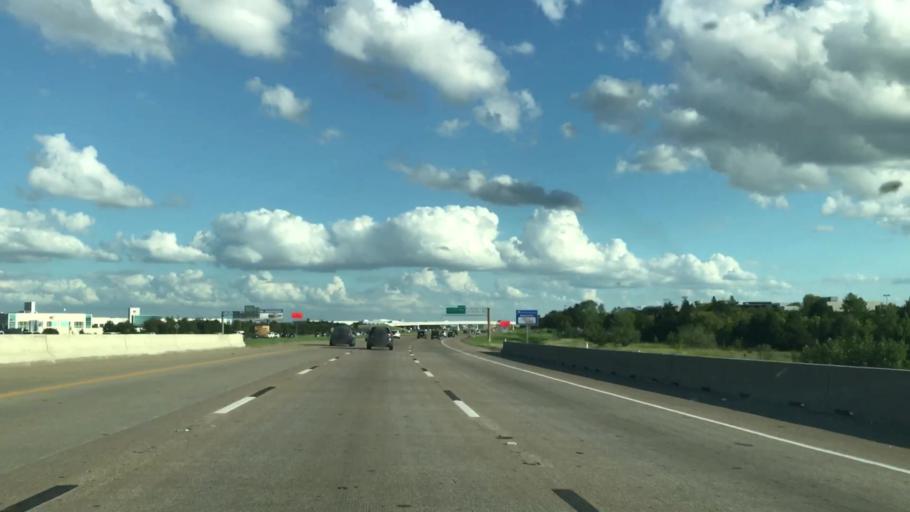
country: US
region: Texas
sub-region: Dallas County
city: Coppell
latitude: 32.9412
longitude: -97.0142
